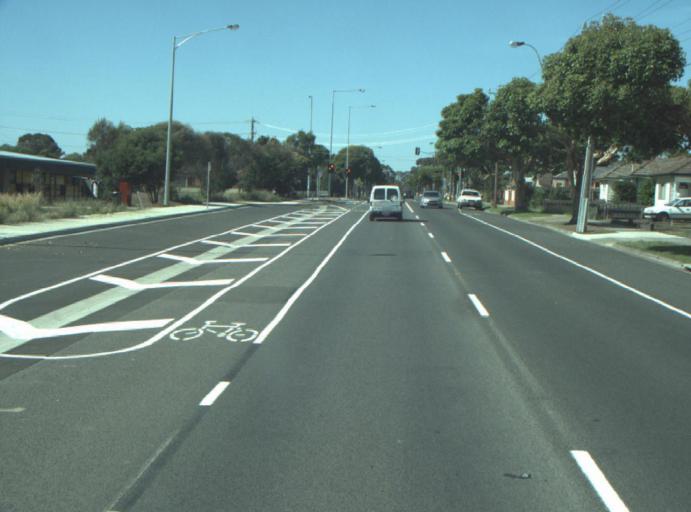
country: AU
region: Victoria
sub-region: Greater Geelong
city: Hamlyn Heights
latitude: -38.1245
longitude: 144.3276
